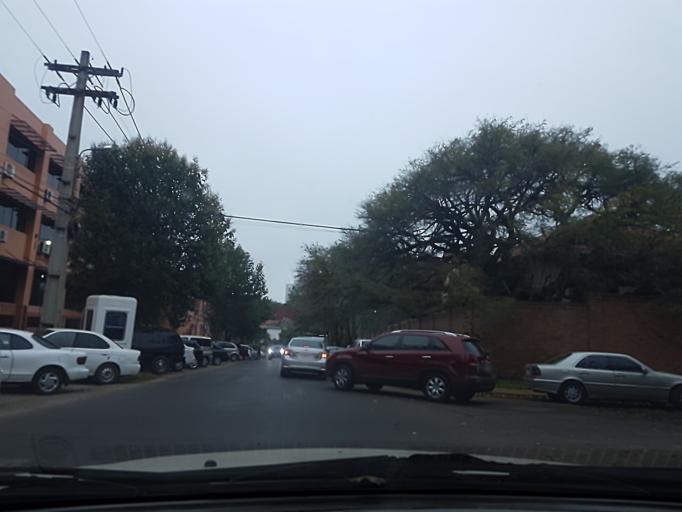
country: PY
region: Central
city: Fernando de la Mora
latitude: -25.2775
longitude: -57.5621
